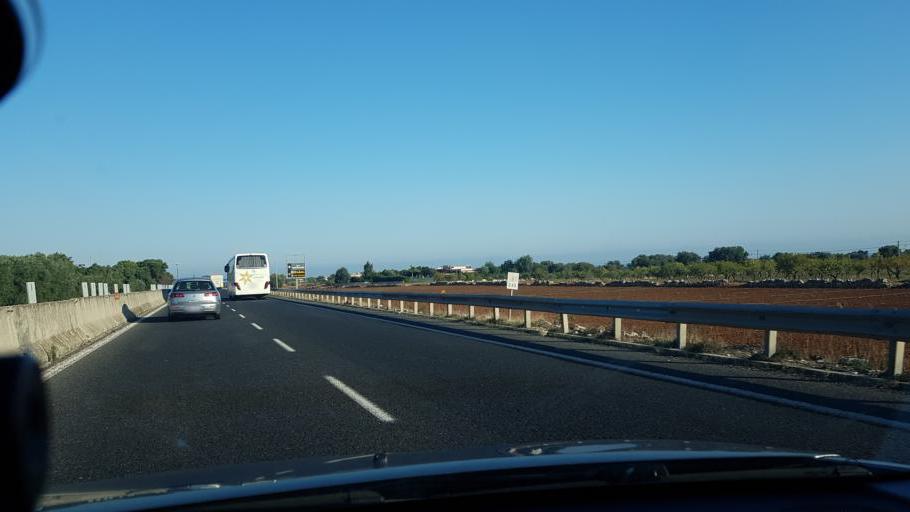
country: IT
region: Apulia
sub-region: Provincia di Bari
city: Monopoli
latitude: 40.9122
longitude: 17.3215
